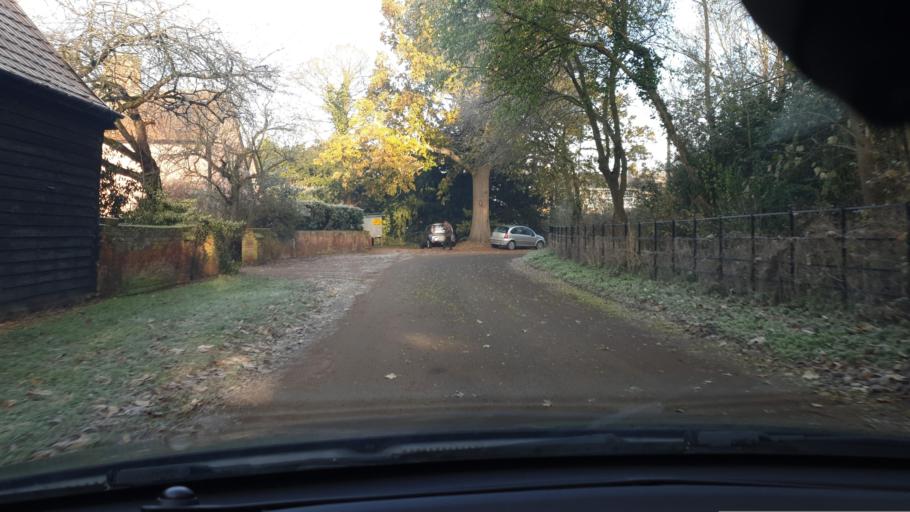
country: GB
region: England
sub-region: Essex
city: Mistley
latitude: 51.9891
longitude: 1.1117
